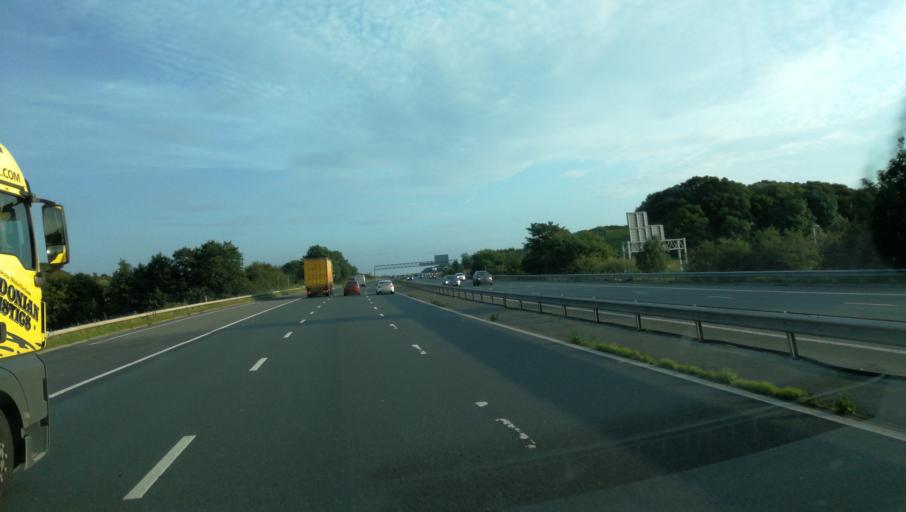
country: GB
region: England
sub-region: Lancashire
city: Bolton le Sands
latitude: 54.0692
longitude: -2.7707
